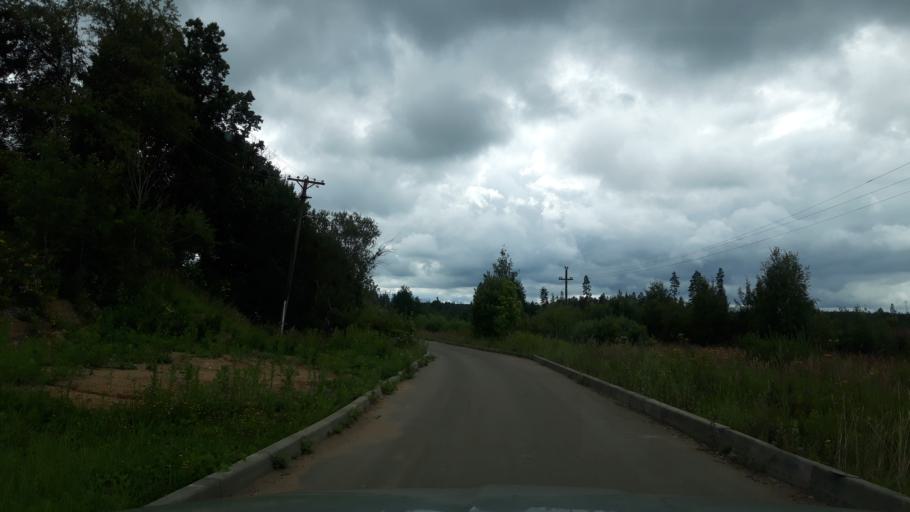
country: RU
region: Moskovskaya
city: Povarovo
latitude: 56.0460
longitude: 37.0549
